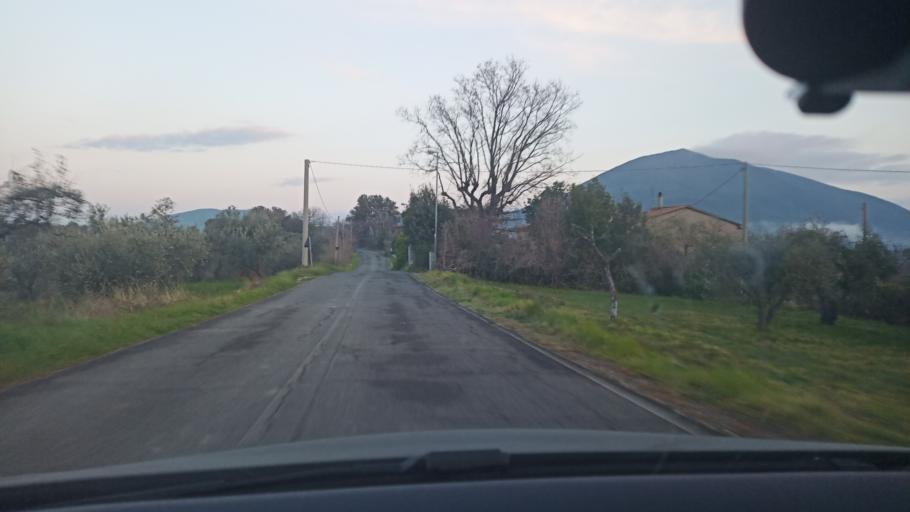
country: IT
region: Latium
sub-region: Provincia di Rieti
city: Montasola
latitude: 42.3643
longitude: 12.6708
